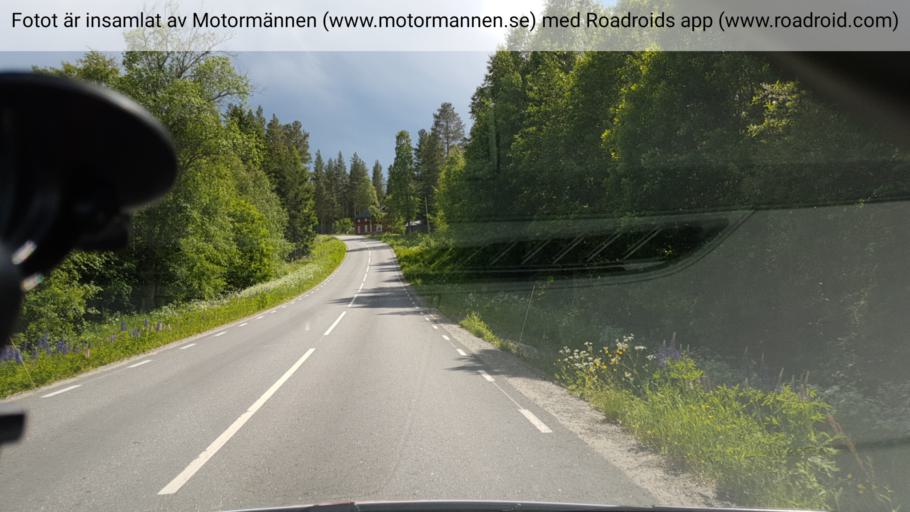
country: SE
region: Gaevleborg
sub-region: Ovanakers Kommun
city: Alfta
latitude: 61.2587
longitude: 16.1244
